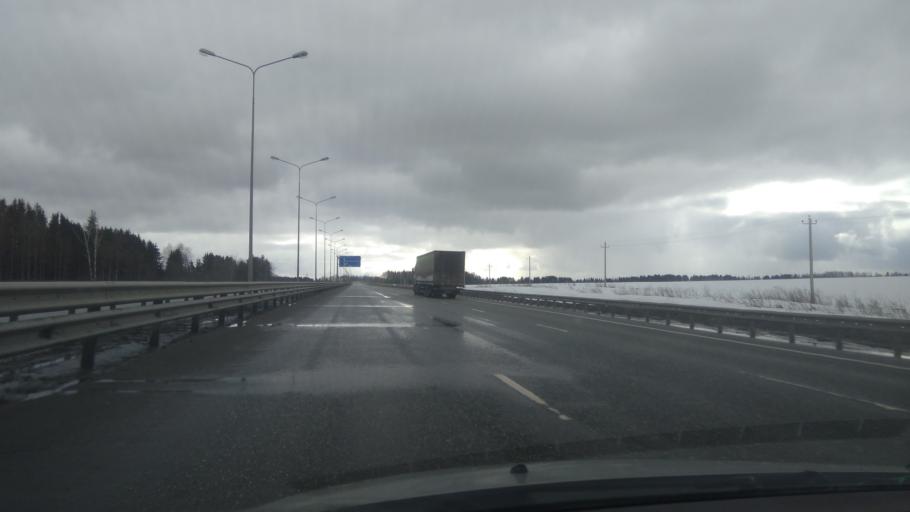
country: RU
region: Perm
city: Bershet'
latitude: 57.6881
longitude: 56.4090
